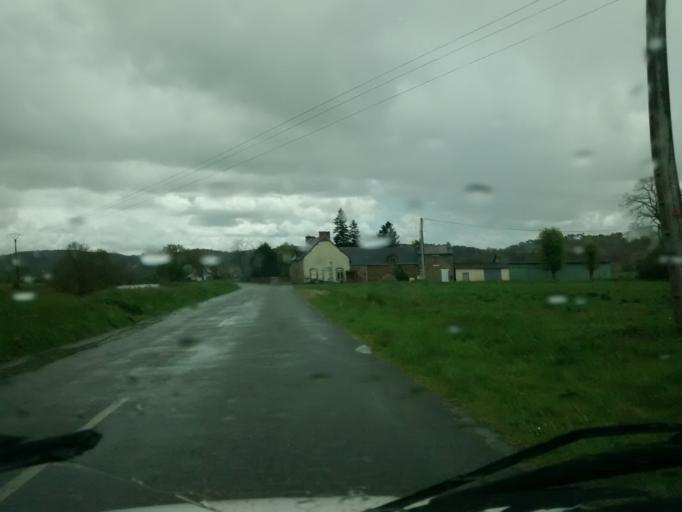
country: FR
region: Brittany
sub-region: Departement du Morbihan
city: Pleucadeuc
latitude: 47.7640
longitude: -2.3178
